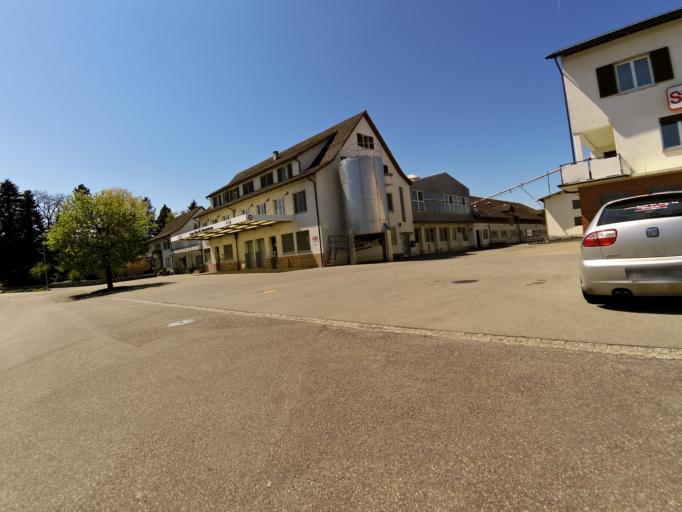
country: CH
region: Thurgau
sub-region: Weinfelden District
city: Berg
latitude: 47.6115
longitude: 9.1682
